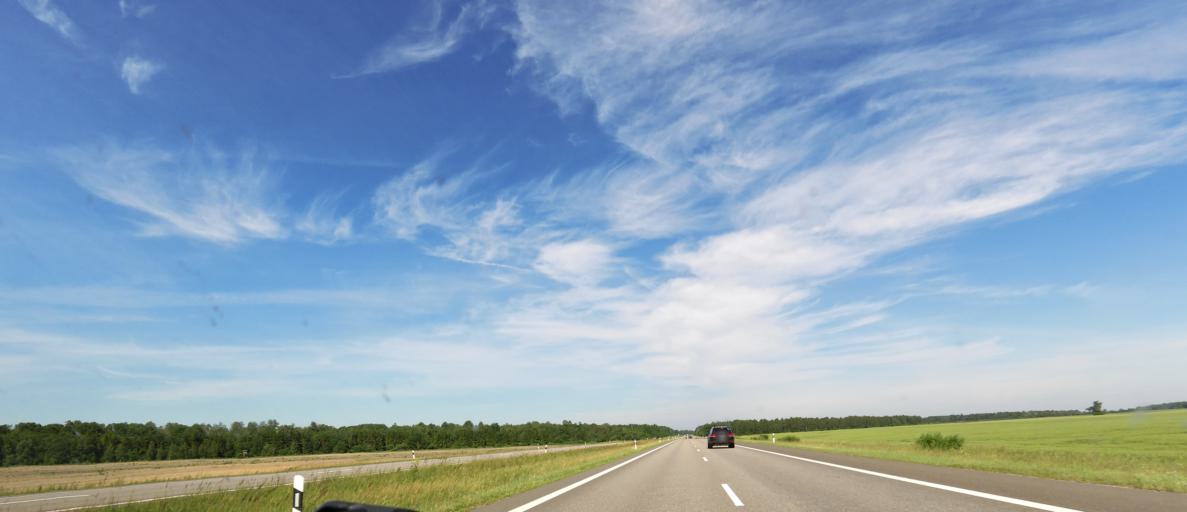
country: LT
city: Ramygala
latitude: 55.5584
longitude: 24.5055
